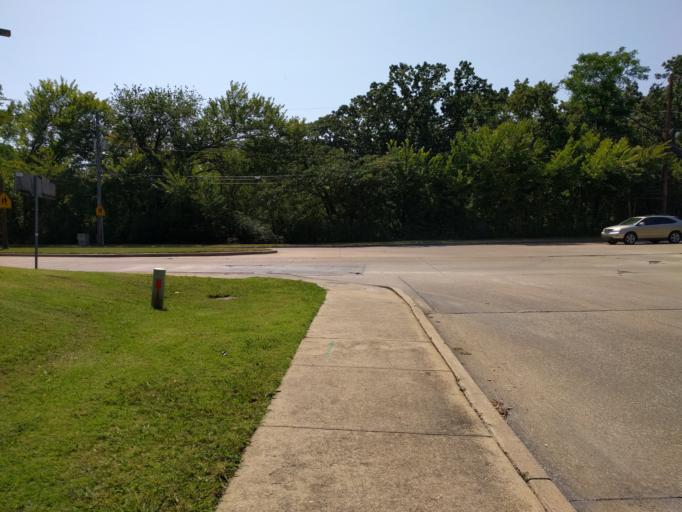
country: US
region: Texas
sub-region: Dallas County
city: Richardson
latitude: 32.9180
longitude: -96.7760
